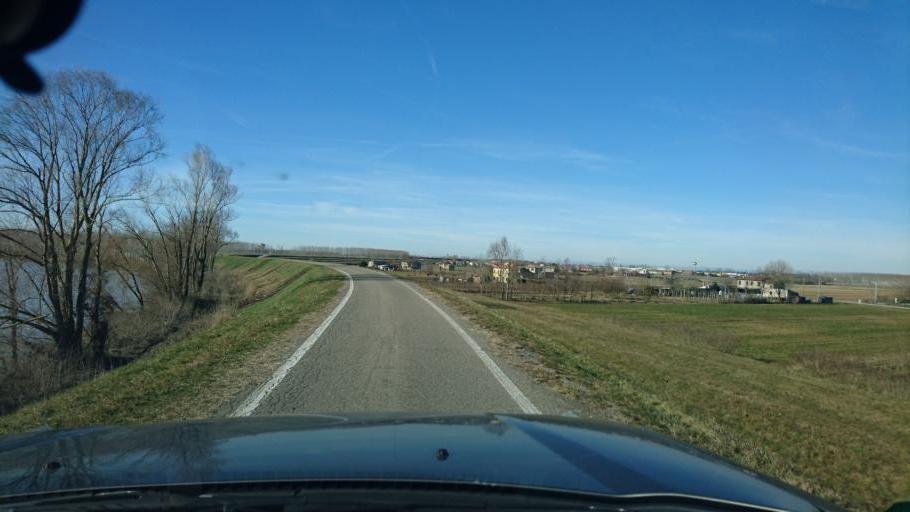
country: IT
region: Veneto
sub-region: Provincia di Rovigo
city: Ariano
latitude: 44.9321
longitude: 12.1370
